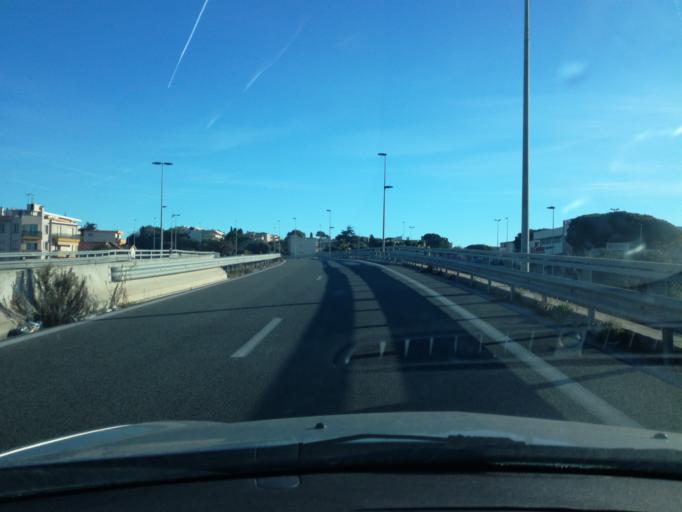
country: FR
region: Provence-Alpes-Cote d'Azur
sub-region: Departement des Alpes-Maritimes
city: Antibes
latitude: 43.5776
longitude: 7.1046
